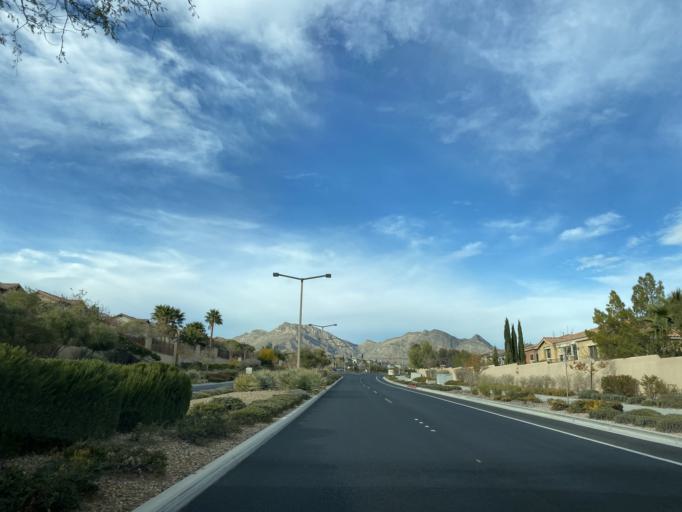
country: US
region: Nevada
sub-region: Clark County
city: Summerlin South
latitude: 36.1691
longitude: -115.3546
